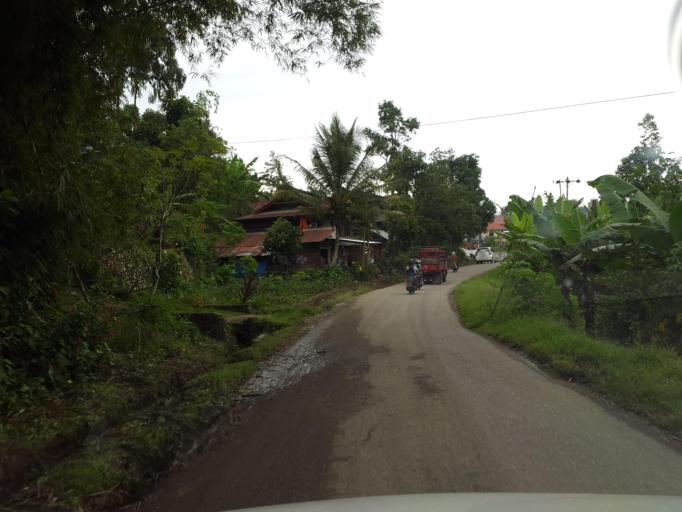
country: ID
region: South Sulawesi
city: Rantepang
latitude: -2.9394
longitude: 119.9367
